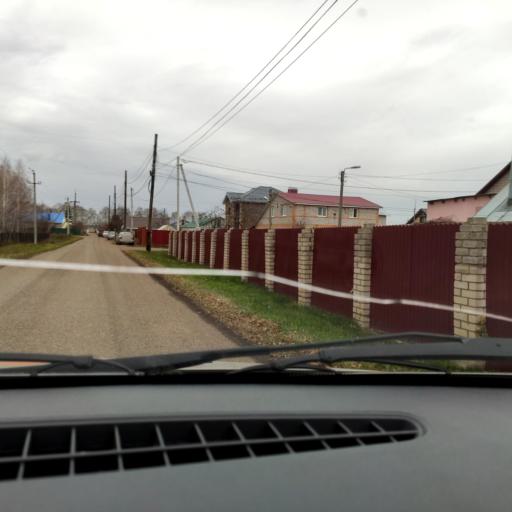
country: RU
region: Bashkortostan
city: Ufa
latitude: 54.8339
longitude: 56.0004
